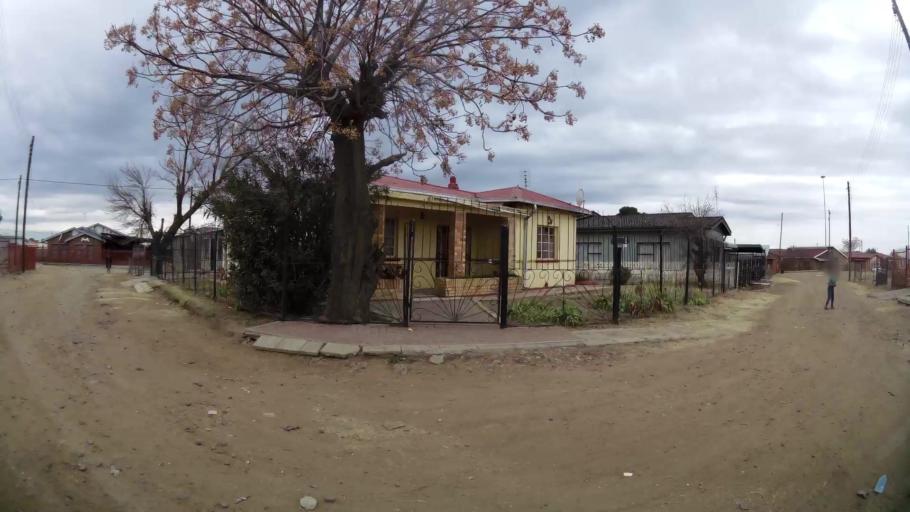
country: ZA
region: Orange Free State
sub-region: Fezile Dabi District Municipality
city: Kroonstad
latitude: -27.6488
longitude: 27.2071
